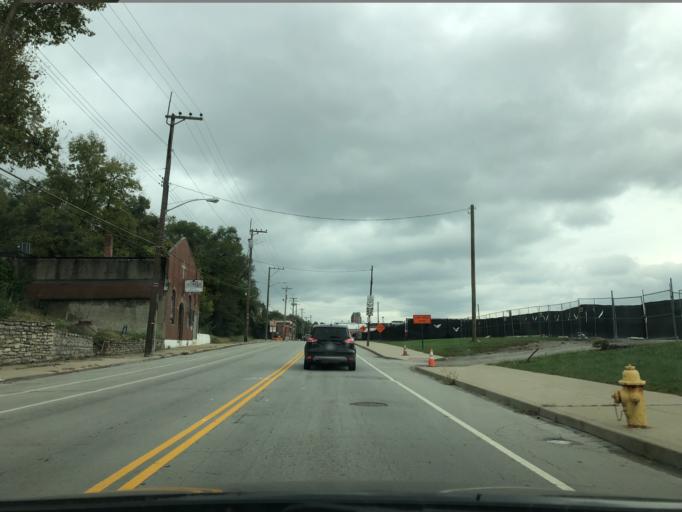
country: US
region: Kentucky
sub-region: Campbell County
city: Dayton
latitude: 39.1230
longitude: -84.4566
